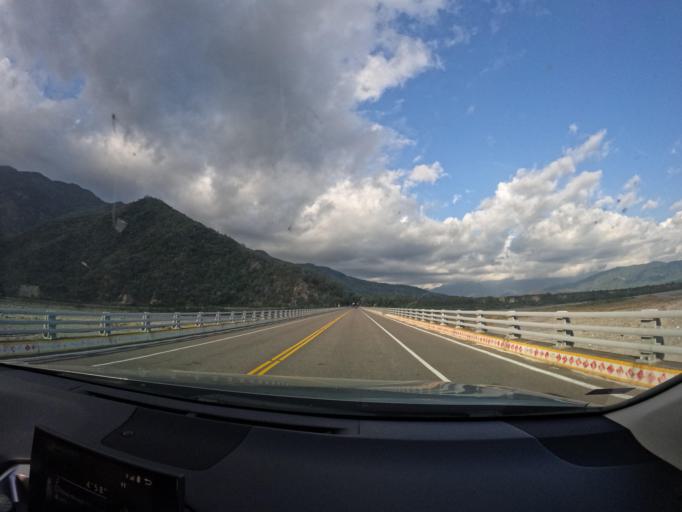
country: TW
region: Taiwan
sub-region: Taitung
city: Taitung
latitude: 23.1244
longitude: 121.1680
